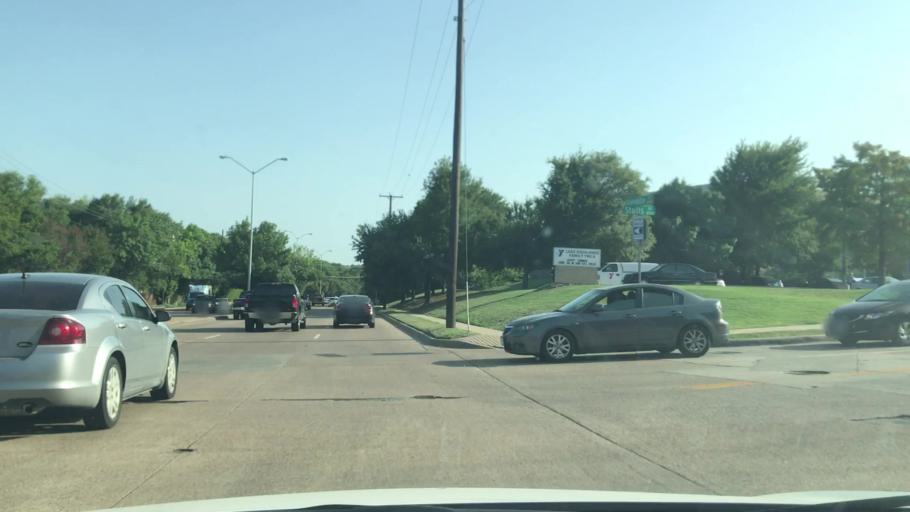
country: US
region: Texas
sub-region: Dallas County
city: Richardson
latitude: 32.9048
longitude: -96.7486
